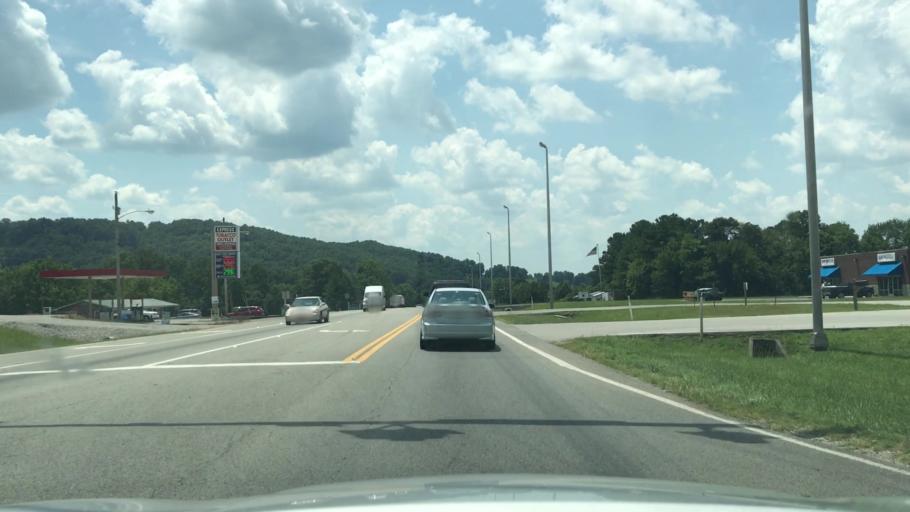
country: US
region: Tennessee
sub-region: Overton County
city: Livingston
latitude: 36.3863
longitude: -85.3348
